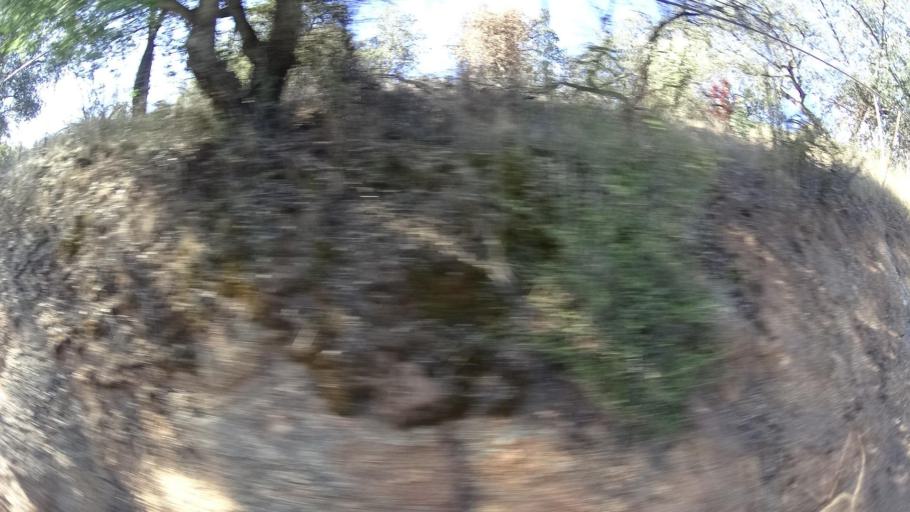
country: MX
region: Baja California
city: Tecate
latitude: 32.6744
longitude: -116.7109
